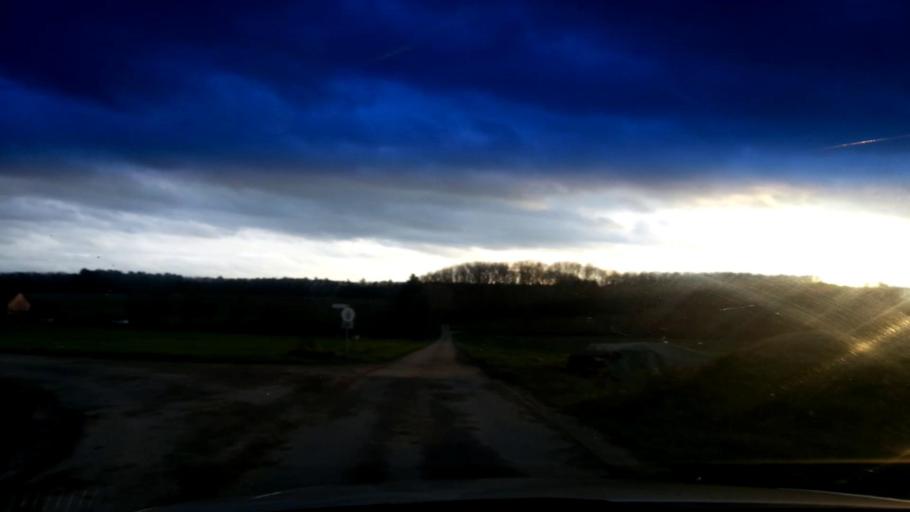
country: DE
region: Bavaria
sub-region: Upper Franconia
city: Schesslitz
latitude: 49.9975
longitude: 10.9903
